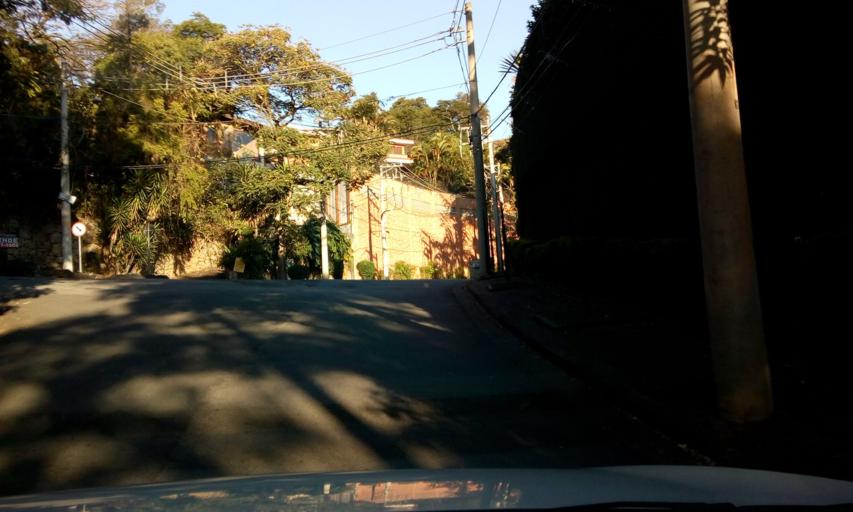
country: BR
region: Sao Paulo
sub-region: Sao Paulo
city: Sao Paulo
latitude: -23.5952
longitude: -46.7035
